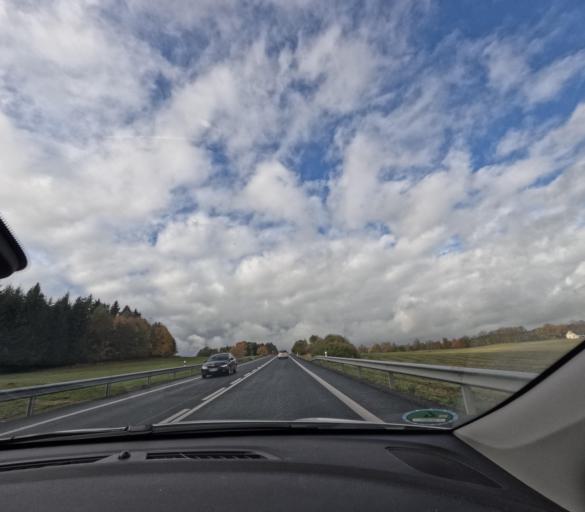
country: CZ
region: Karlovarsky
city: Bochov
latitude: 50.1447
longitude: 13.0851
